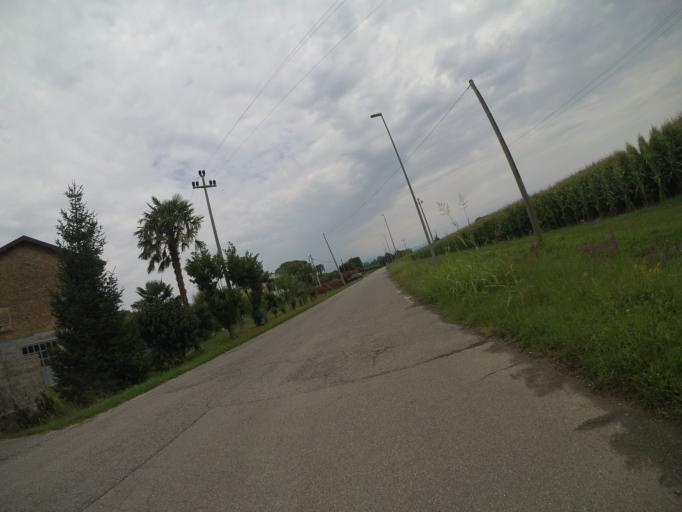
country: IT
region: Friuli Venezia Giulia
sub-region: Provincia di Udine
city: Camino al Tagliamento
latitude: 45.9167
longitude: 12.9550
